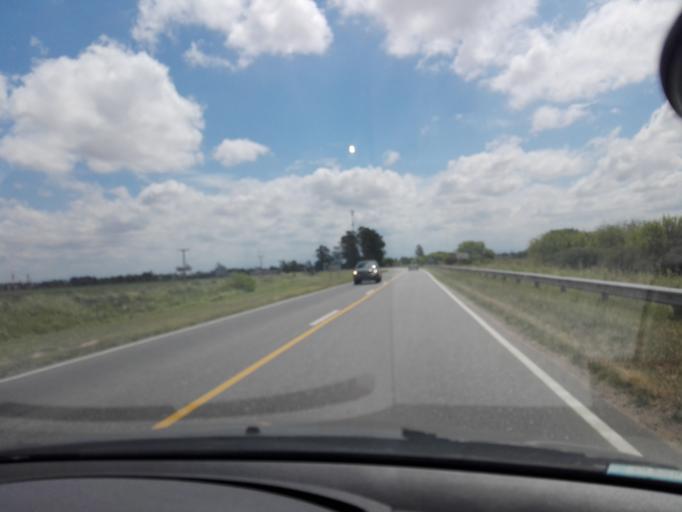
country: AR
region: Cordoba
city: Toledo
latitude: -31.6474
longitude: -64.0790
